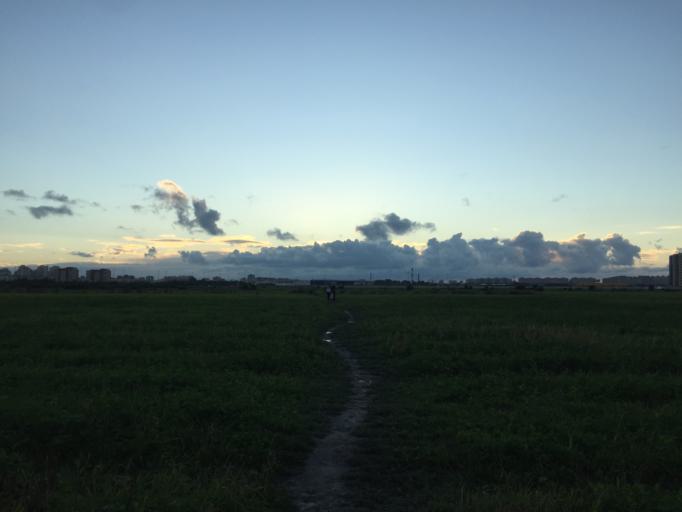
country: RU
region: St.-Petersburg
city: Grazhdanka
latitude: 60.0556
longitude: 30.4130
